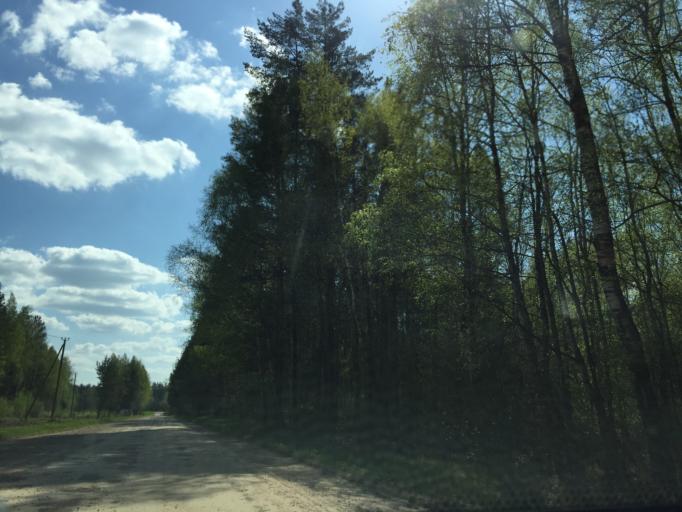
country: LV
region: Vecumnieki
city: Vecumnieki
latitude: 56.4812
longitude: 24.5344
